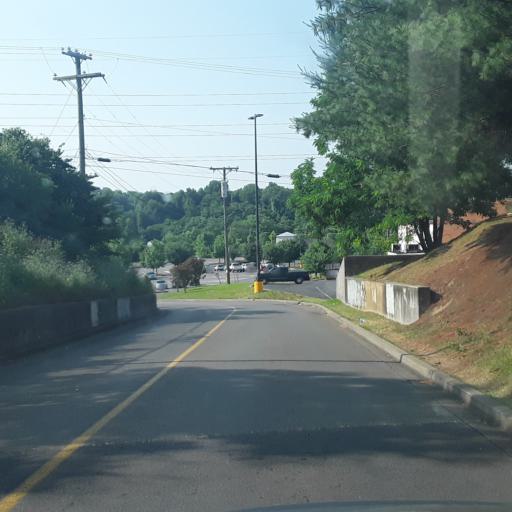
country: US
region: Tennessee
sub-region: Williamson County
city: Brentwood Estates
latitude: 36.0443
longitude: -86.7121
